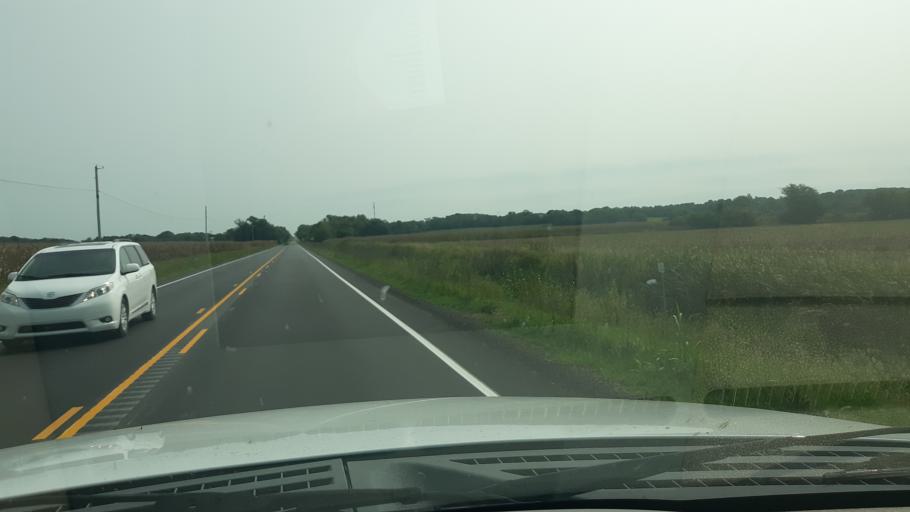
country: US
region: Indiana
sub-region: Gibson County
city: Princeton
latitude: 38.3557
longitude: -87.6360
